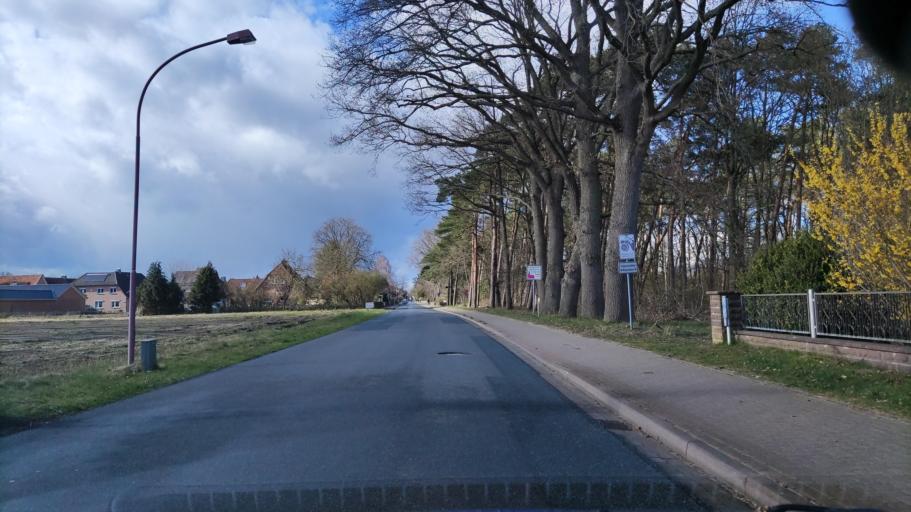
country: DE
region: Lower Saxony
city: Hermannsburg
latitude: 52.8222
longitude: 10.0942
